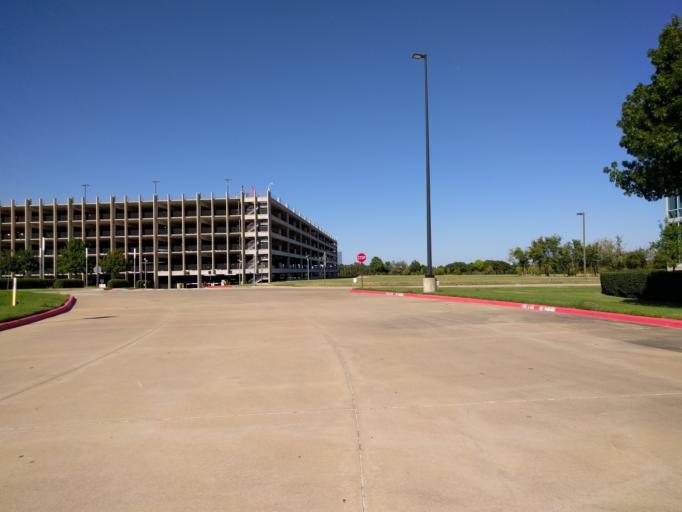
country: US
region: Texas
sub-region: Collin County
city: Plano
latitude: 32.9864
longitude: -96.7059
